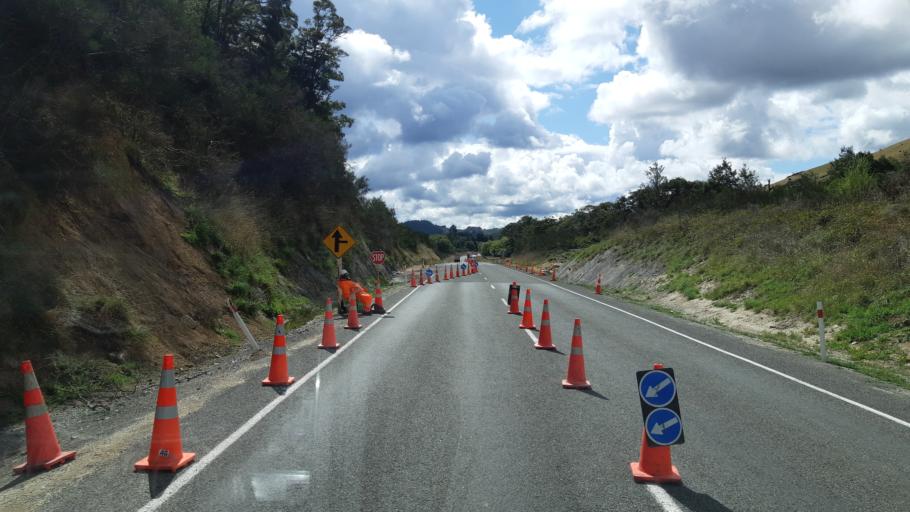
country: NZ
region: Tasman
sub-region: Tasman District
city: Wakefield
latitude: -41.6541
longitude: 172.6444
